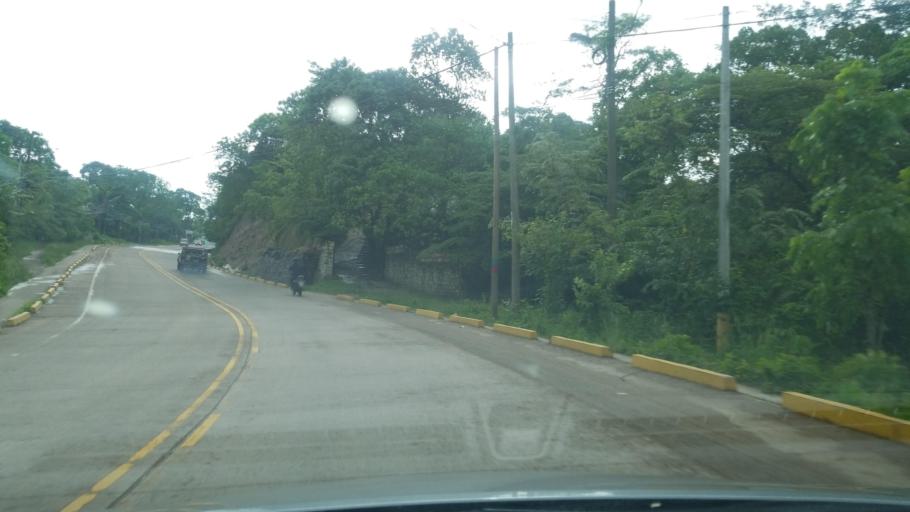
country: HN
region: Copan
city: Copan
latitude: 14.8422
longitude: -89.1640
